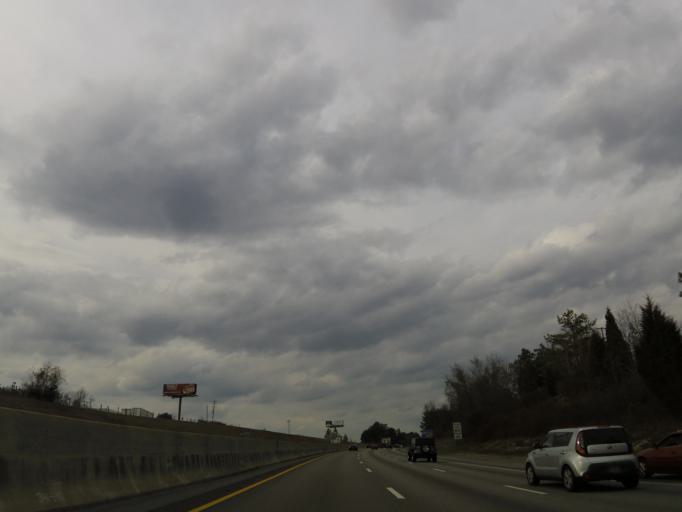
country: US
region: South Carolina
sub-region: Lexington County
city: Cayce
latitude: 33.9396
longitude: -81.0872
